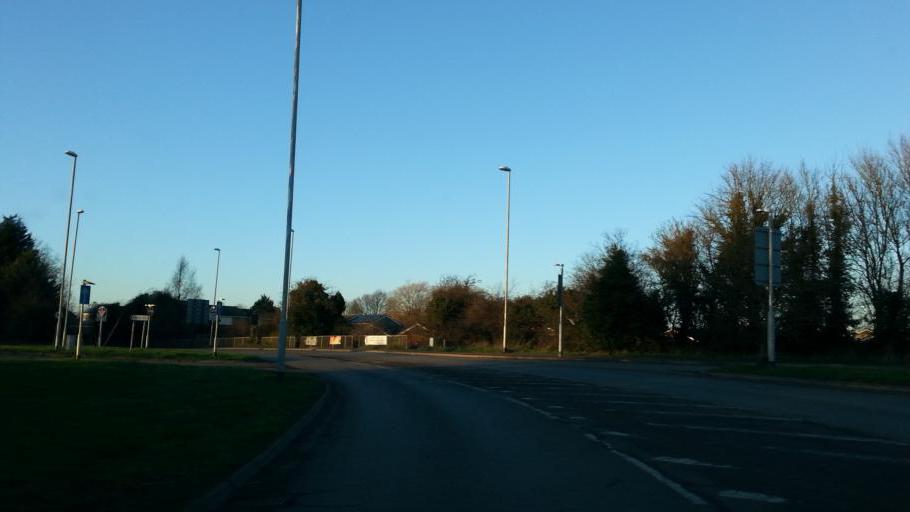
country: GB
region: England
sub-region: Cambridgeshire
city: Hemingford Grey
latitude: 52.2956
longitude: -0.0643
